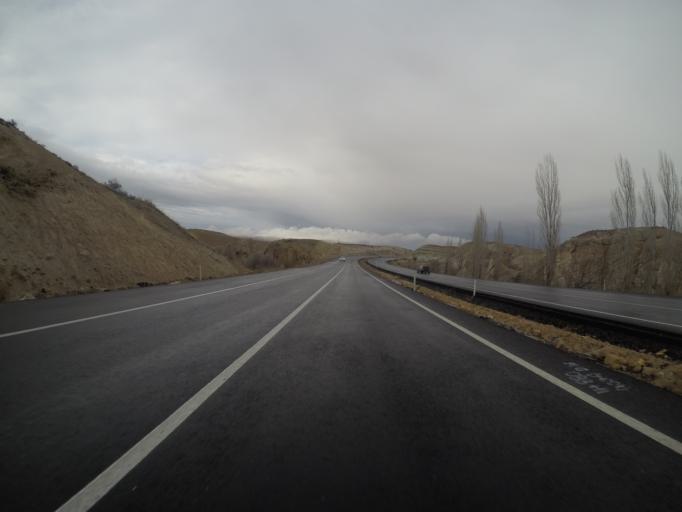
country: TR
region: Nevsehir
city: Avanos
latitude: 38.6922
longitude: 34.8169
